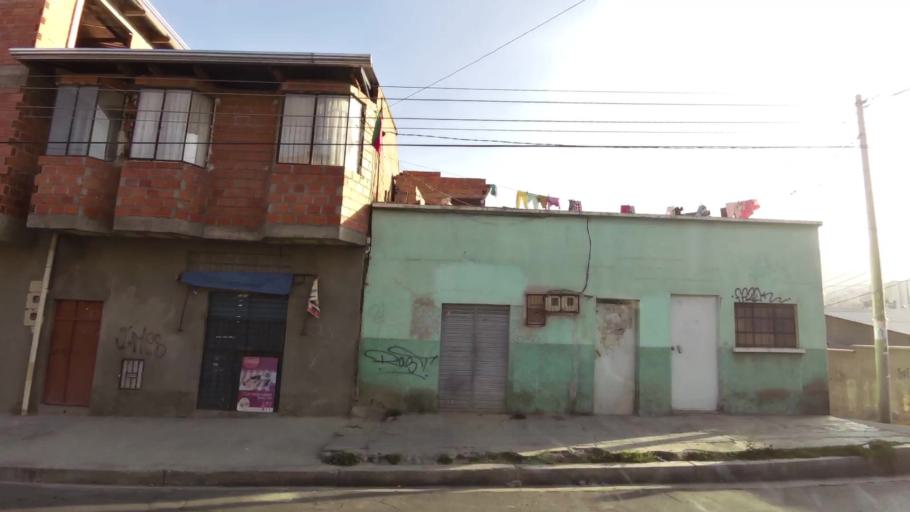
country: BO
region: La Paz
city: La Paz
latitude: -16.5133
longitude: -68.1138
